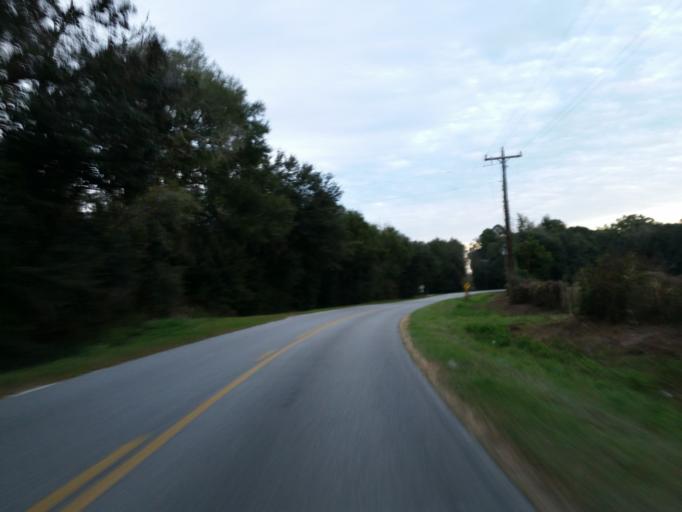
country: US
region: Florida
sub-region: Hamilton County
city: Jasper
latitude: 30.5258
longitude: -83.0720
